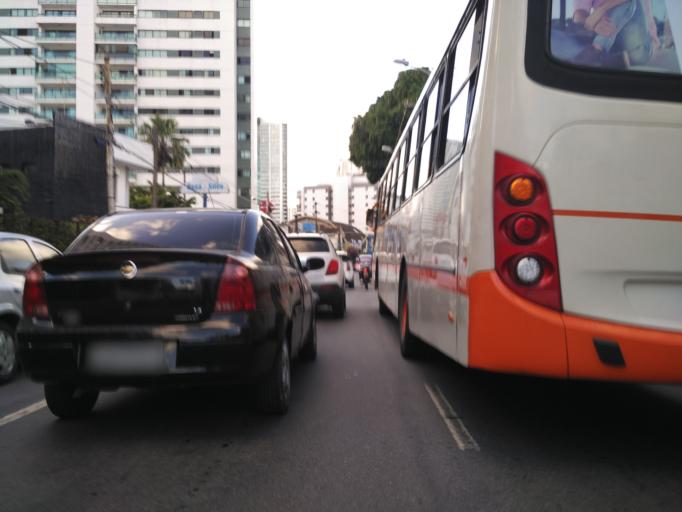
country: BR
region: Pernambuco
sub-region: Recife
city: Recife
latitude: -8.0379
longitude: -34.9008
